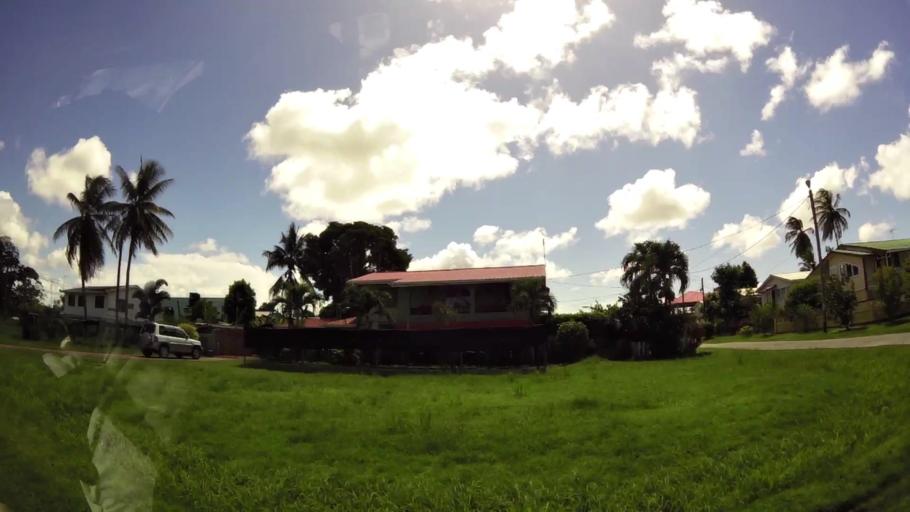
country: GY
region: Demerara-Mahaica
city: Georgetown
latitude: 6.7839
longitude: -58.1412
